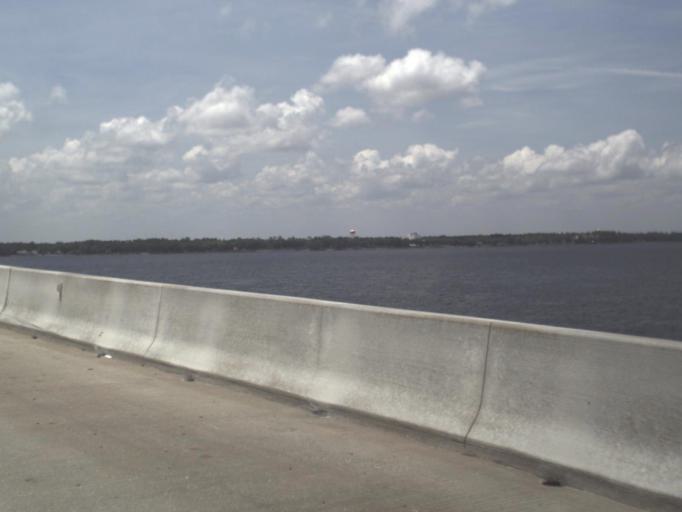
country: US
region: Florida
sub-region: Clay County
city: Orange Park
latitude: 30.1900
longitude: -81.6624
